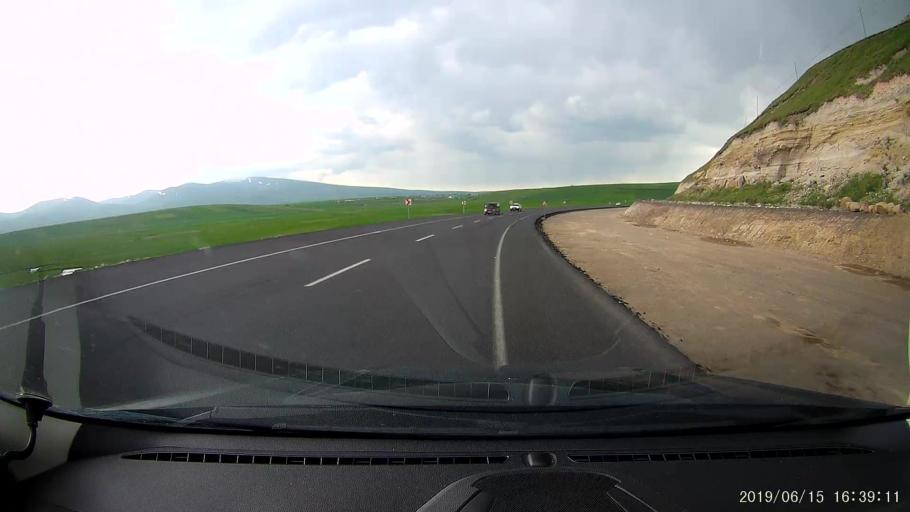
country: TR
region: Ardahan
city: Haskoy
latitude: 40.9856
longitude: 42.8950
